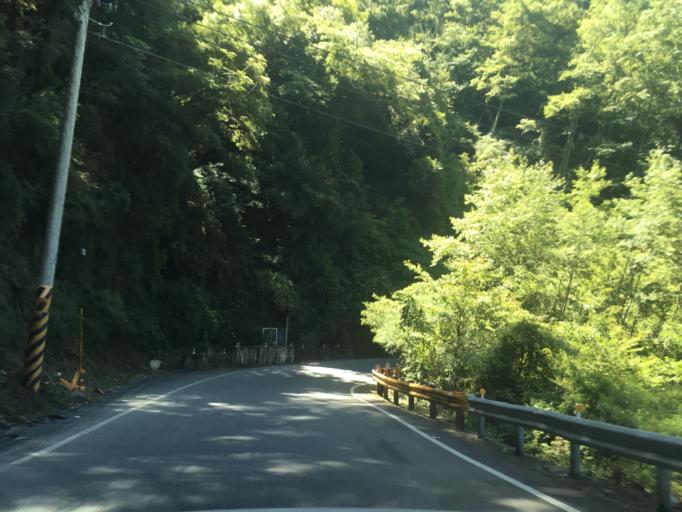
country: TW
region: Taiwan
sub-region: Nantou
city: Puli
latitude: 24.2142
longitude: 121.2675
